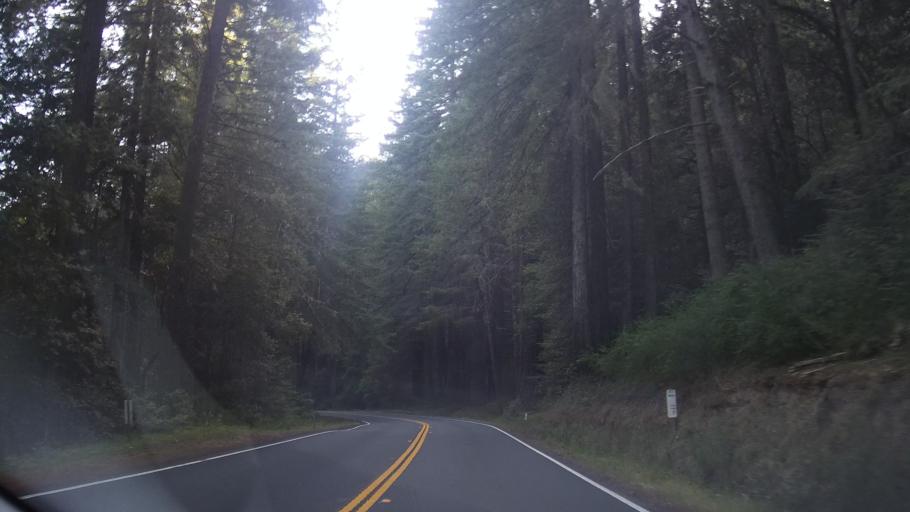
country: US
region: California
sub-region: Mendocino County
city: Brooktrails
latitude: 39.3522
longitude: -123.5611
